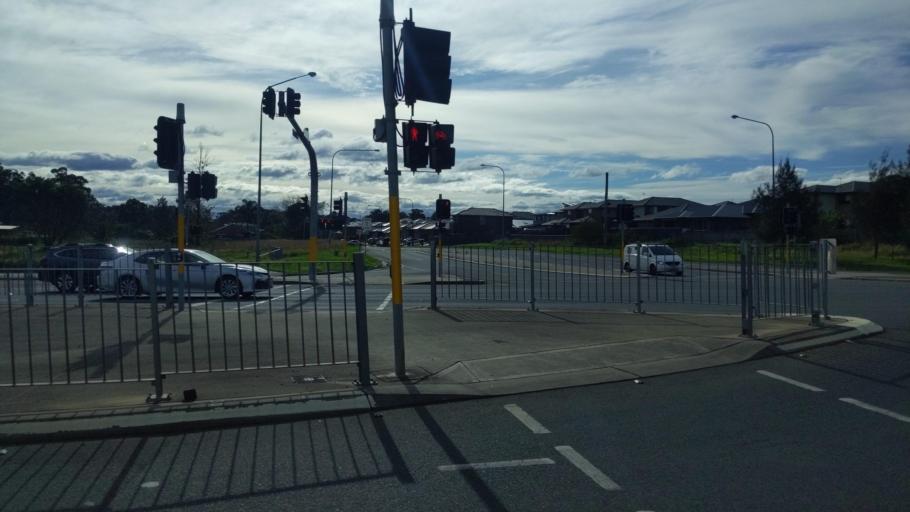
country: AU
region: New South Wales
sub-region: Blacktown
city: Riverstone
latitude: -33.7043
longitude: 150.8664
